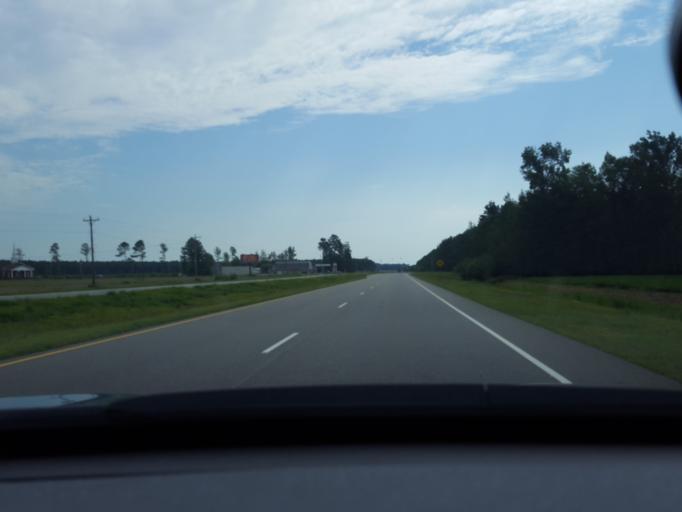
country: US
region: North Carolina
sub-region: Chowan County
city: Edenton
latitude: 36.0385
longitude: -76.7425
